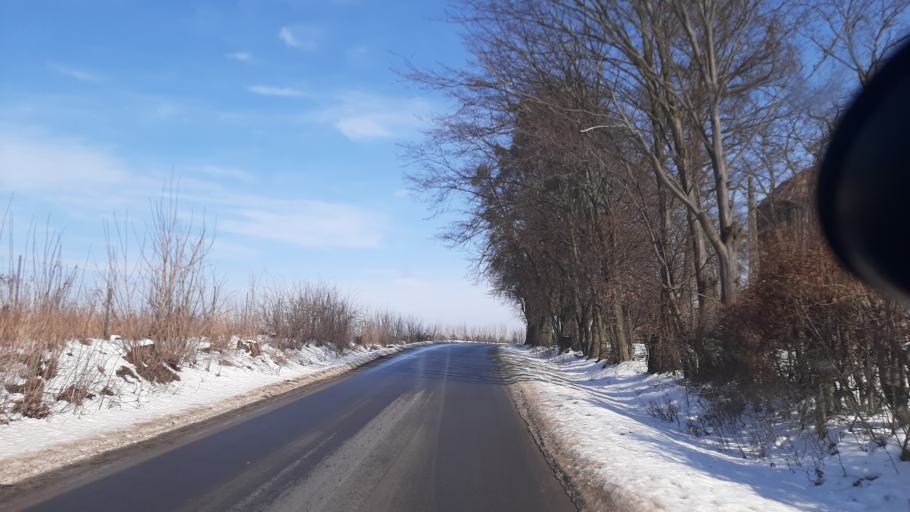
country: PL
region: Lublin Voivodeship
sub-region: Powiat pulawski
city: Wawolnica
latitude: 51.3502
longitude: 22.1128
